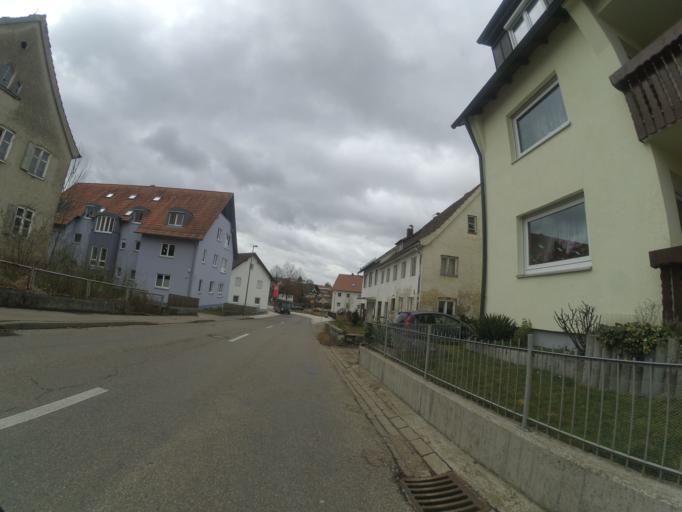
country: DE
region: Bavaria
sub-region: Swabia
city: Vohringen
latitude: 48.2894
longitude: 10.1003
